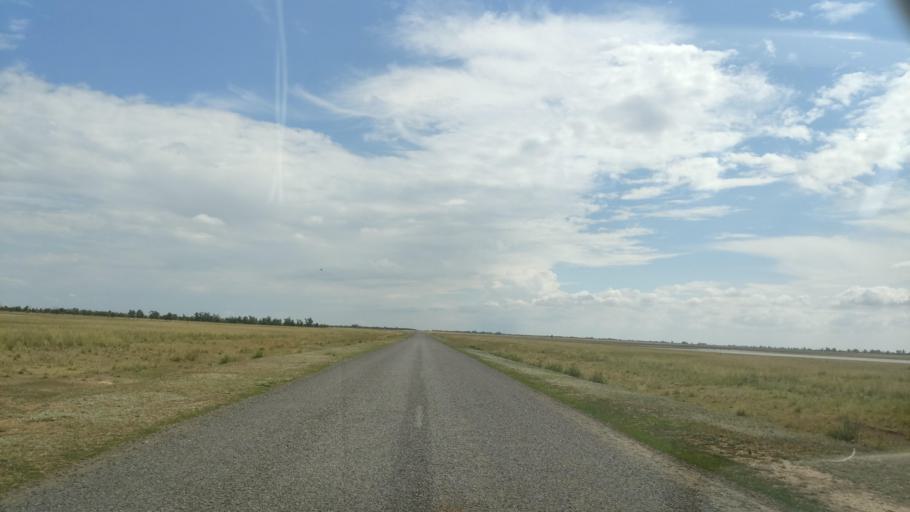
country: KZ
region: Pavlodar
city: Pavlodar
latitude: 52.6355
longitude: 76.9239
